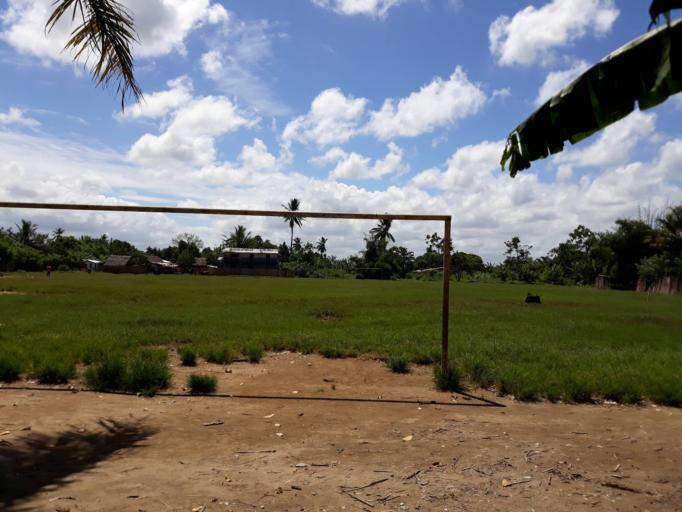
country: MG
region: Atsinanana
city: Ampasimanolotra
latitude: -18.8178
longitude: 49.0711
